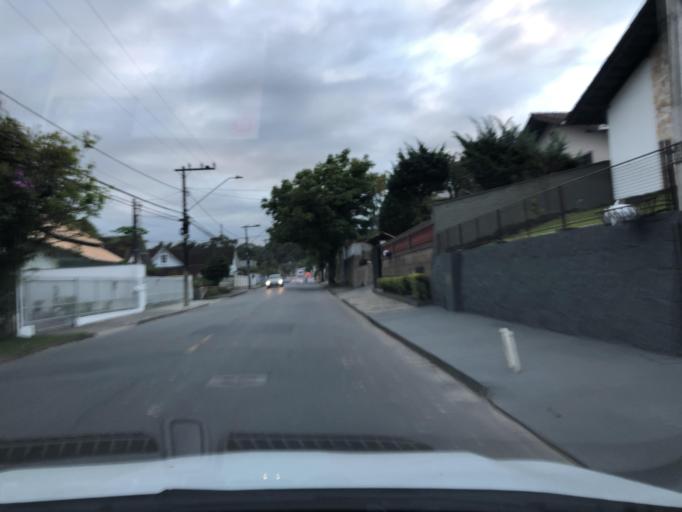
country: BR
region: Santa Catarina
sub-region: Joinville
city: Joinville
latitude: -26.2910
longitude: -48.8744
